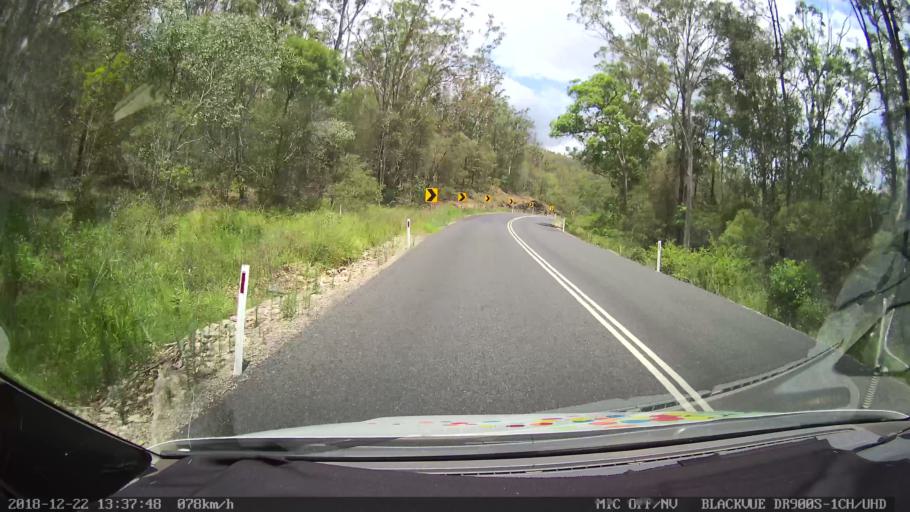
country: AU
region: New South Wales
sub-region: Clarence Valley
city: Coutts Crossing
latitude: -29.8939
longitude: 152.7895
